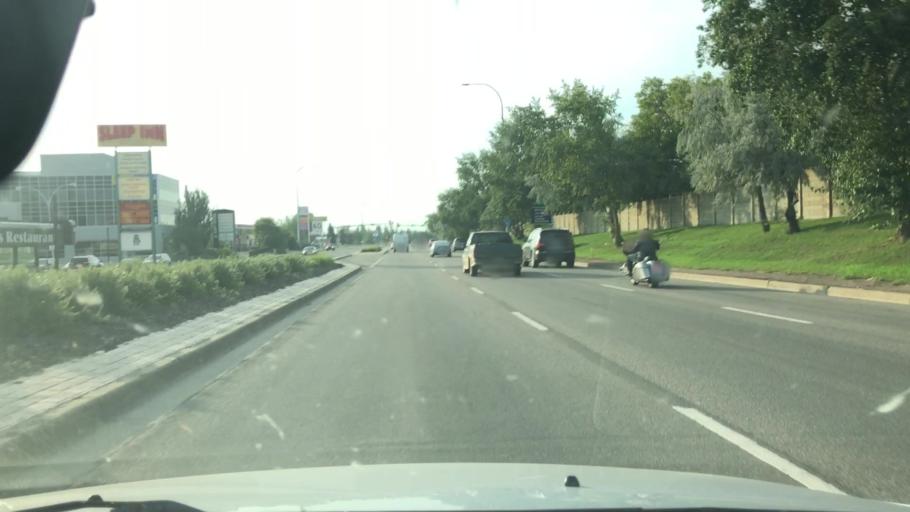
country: CA
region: Alberta
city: St. Albert
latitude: 53.6256
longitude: -113.6159
